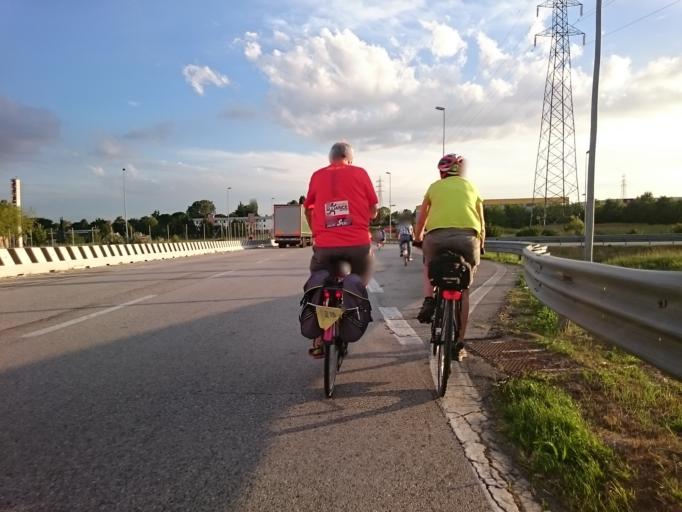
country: IT
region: Veneto
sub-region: Provincia di Padova
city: Ponte San Nicolo
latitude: 45.3817
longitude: 11.9389
